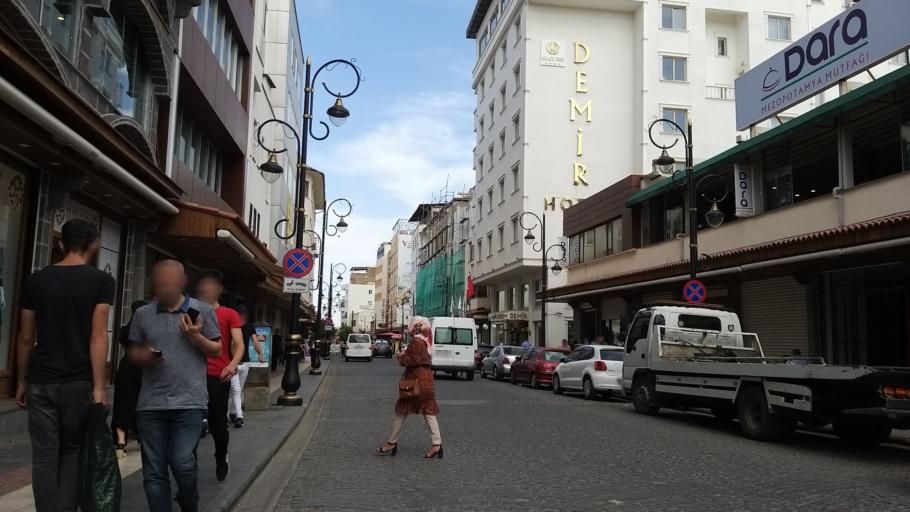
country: TR
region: Diyarbakir
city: Sur
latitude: 37.9149
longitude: 40.2369
